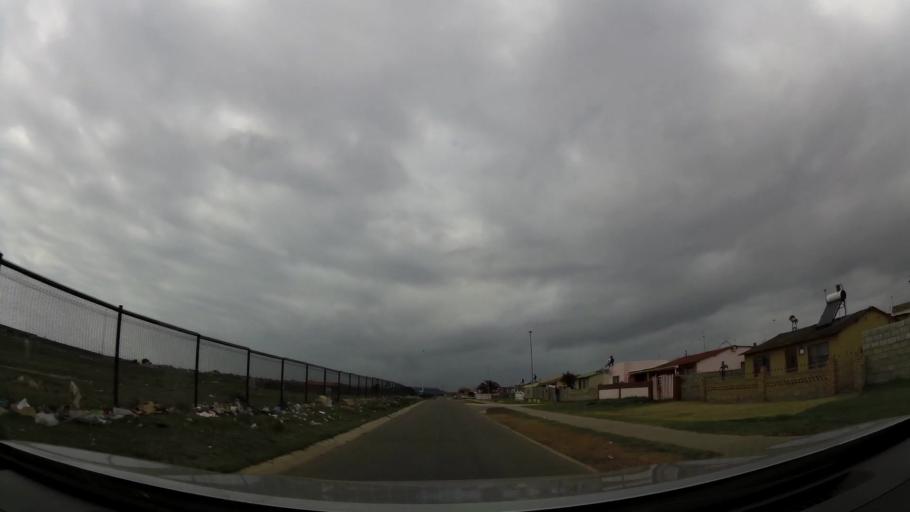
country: ZA
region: Eastern Cape
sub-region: Nelson Mandela Bay Metropolitan Municipality
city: Port Elizabeth
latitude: -33.8756
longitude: 25.5968
